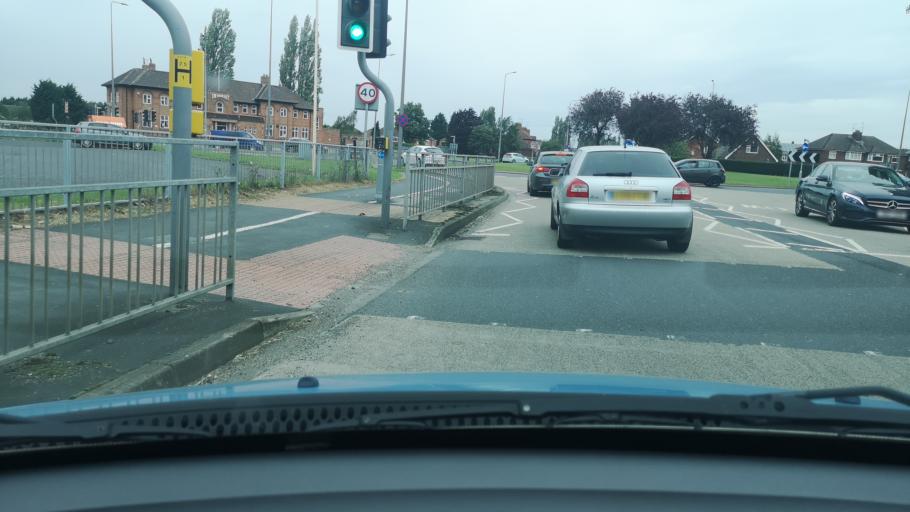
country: GB
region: England
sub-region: North Lincolnshire
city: Scunthorpe
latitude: 53.5896
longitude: -0.6838
